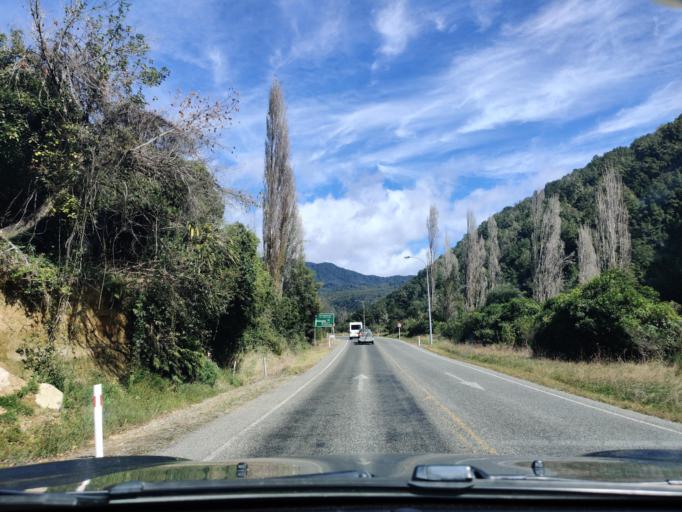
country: NZ
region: West Coast
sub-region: Buller District
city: Westport
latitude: -41.7757
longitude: 172.2224
